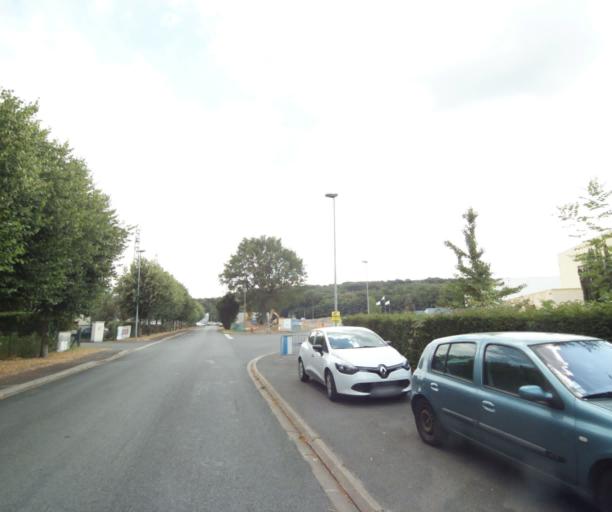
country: FR
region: Ile-de-France
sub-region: Departement de Seine-et-Marne
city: Vulaines-sur-Seine
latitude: 48.4249
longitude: 2.7672
